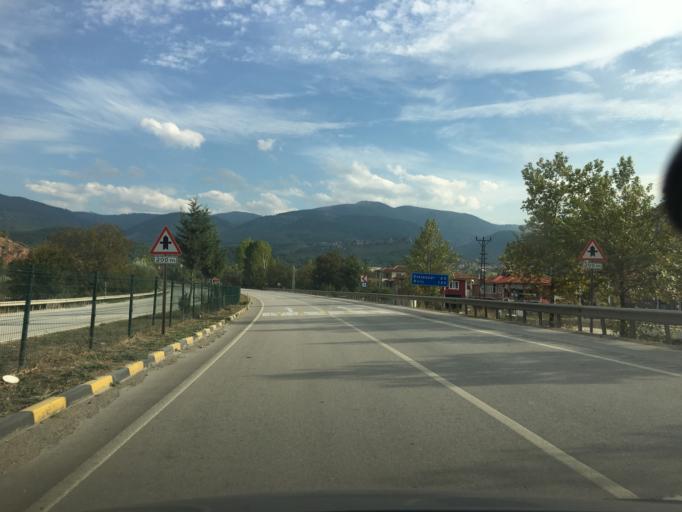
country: TR
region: Karabuk
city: Karabuk
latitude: 41.1018
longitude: 32.6696
